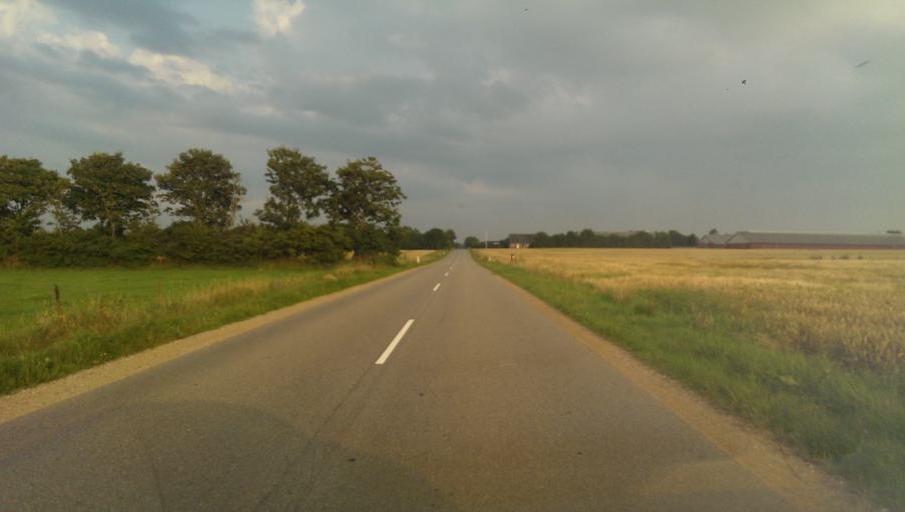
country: DK
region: South Denmark
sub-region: Varde Kommune
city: Varde
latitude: 55.5779
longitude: 8.5661
